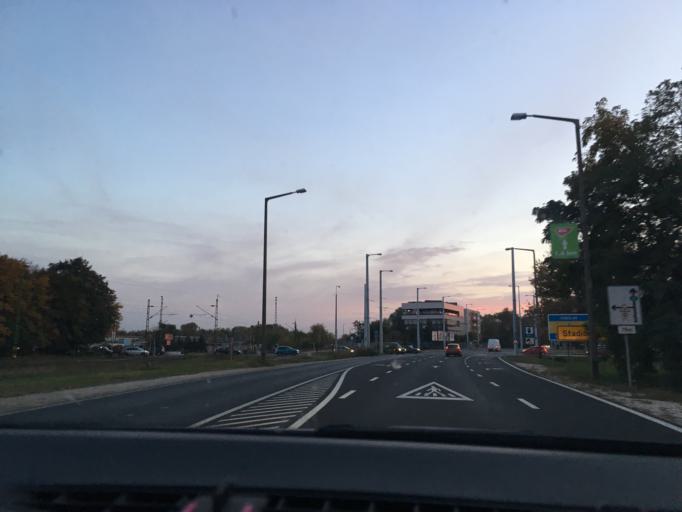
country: HU
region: Hajdu-Bihar
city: Debrecen
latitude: 47.5541
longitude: 21.6500
